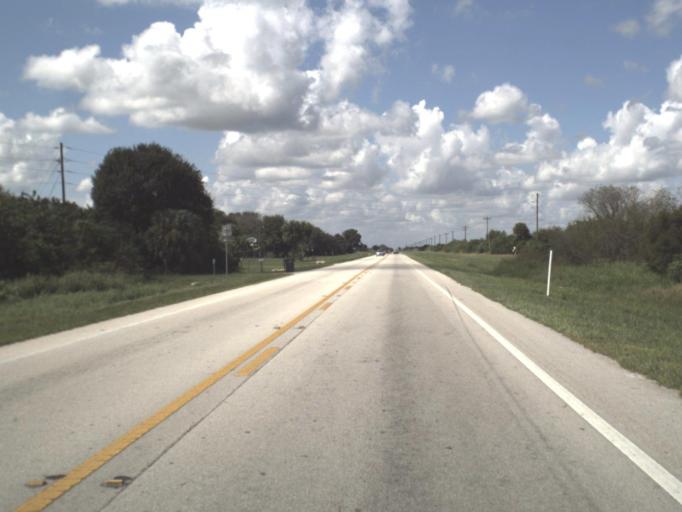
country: US
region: Florida
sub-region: Collier County
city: Immokalee
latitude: 26.4862
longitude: -81.4371
